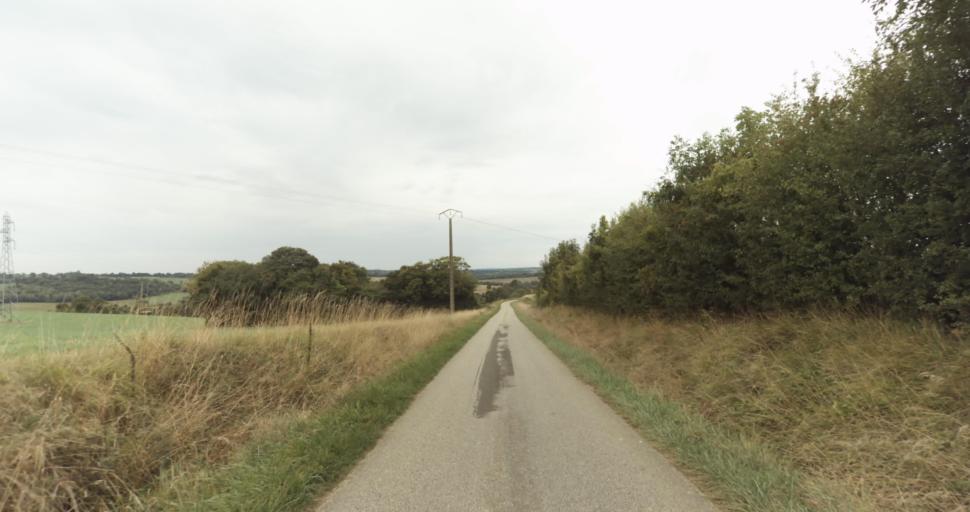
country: FR
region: Lower Normandy
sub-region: Departement de l'Orne
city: Gace
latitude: 48.7498
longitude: 0.3520
